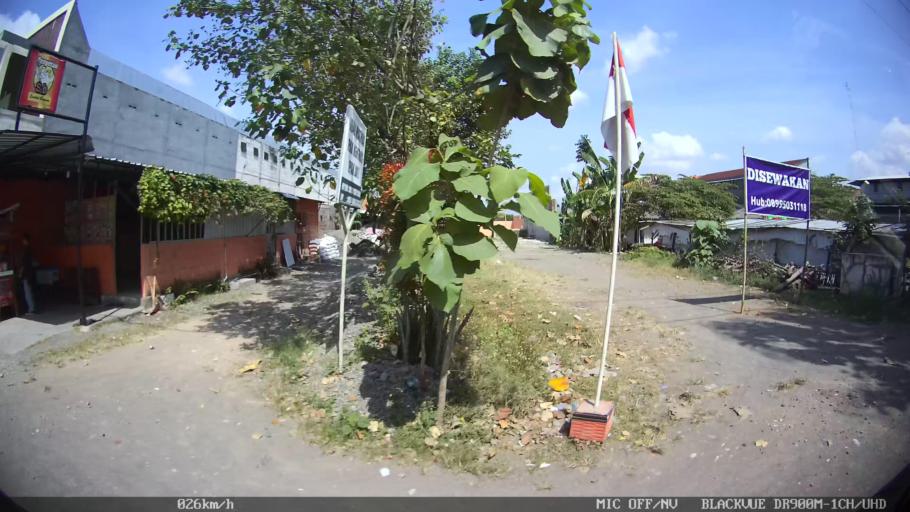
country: ID
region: Daerah Istimewa Yogyakarta
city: Sewon
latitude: -7.8334
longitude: 110.3811
